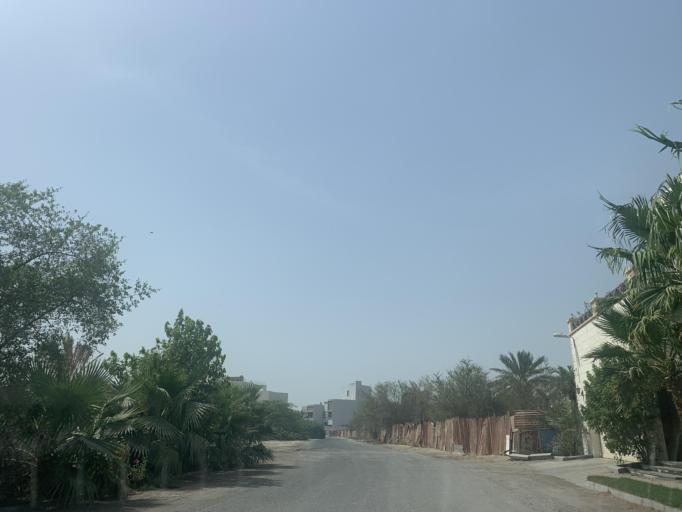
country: BH
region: Northern
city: Madinat `Isa
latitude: 26.1871
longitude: 50.4929
